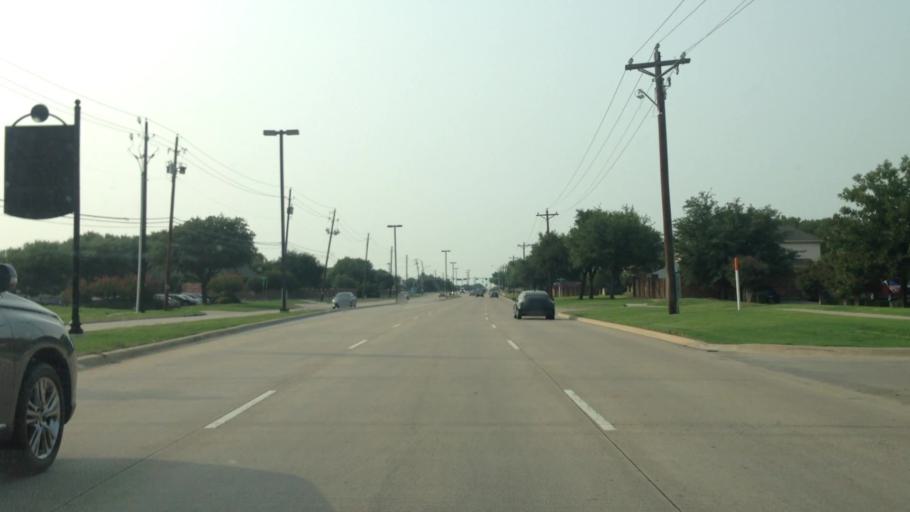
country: US
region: Texas
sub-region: Dallas County
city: Carrollton
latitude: 33.0125
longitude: -96.9118
